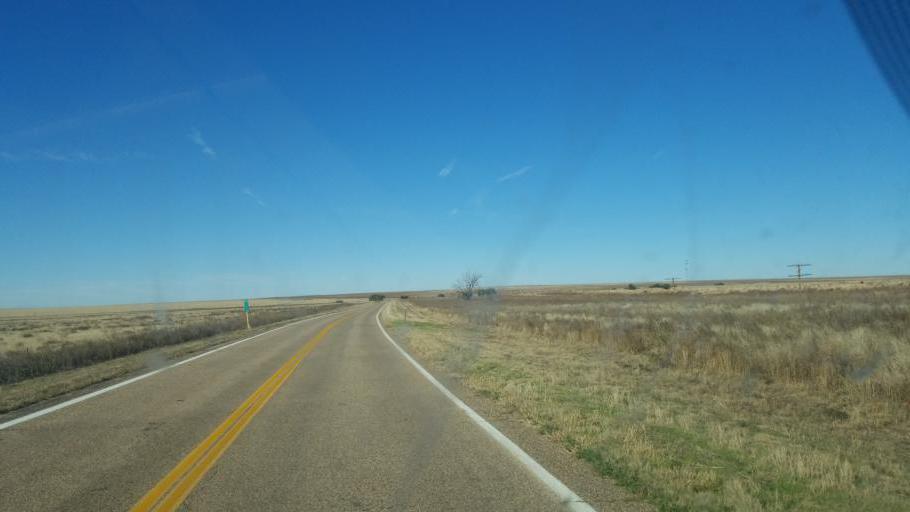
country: US
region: Colorado
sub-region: Bent County
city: Las Animas
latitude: 38.2834
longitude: -103.4307
